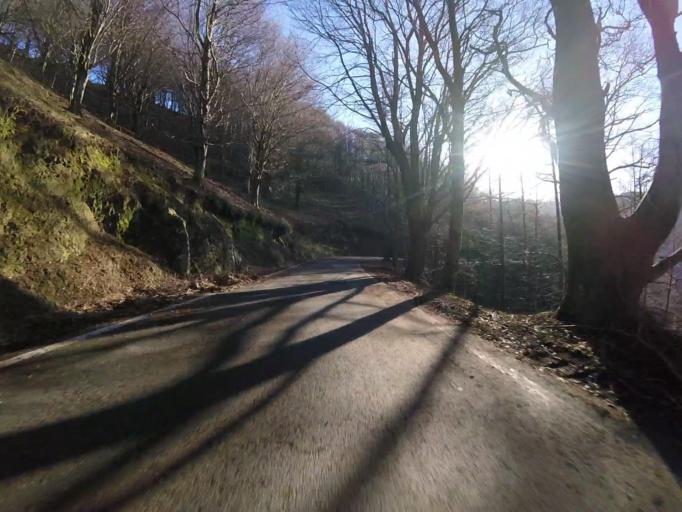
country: ES
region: Navarre
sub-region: Provincia de Navarra
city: Lesaka
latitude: 43.2638
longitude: -1.7619
